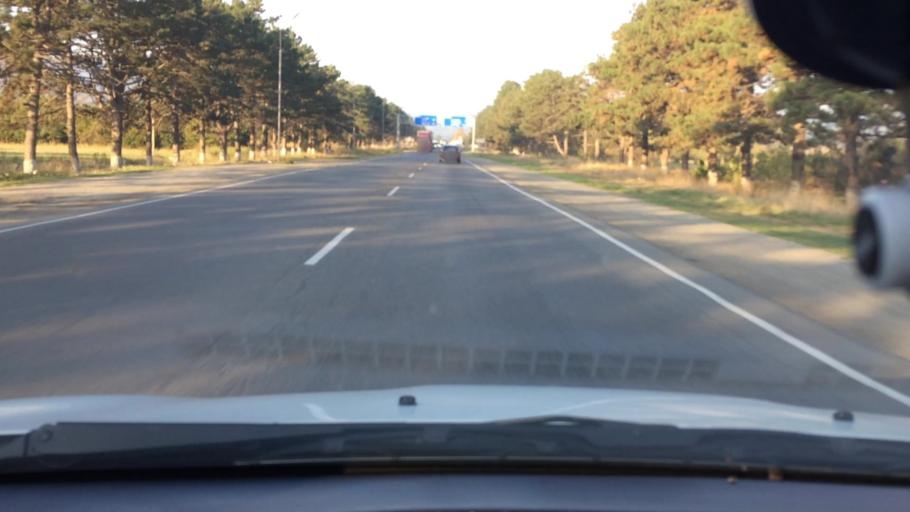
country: GE
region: Shida Kartli
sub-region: Khashuris Raioni
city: Khashuri
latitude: 41.9929
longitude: 43.6320
